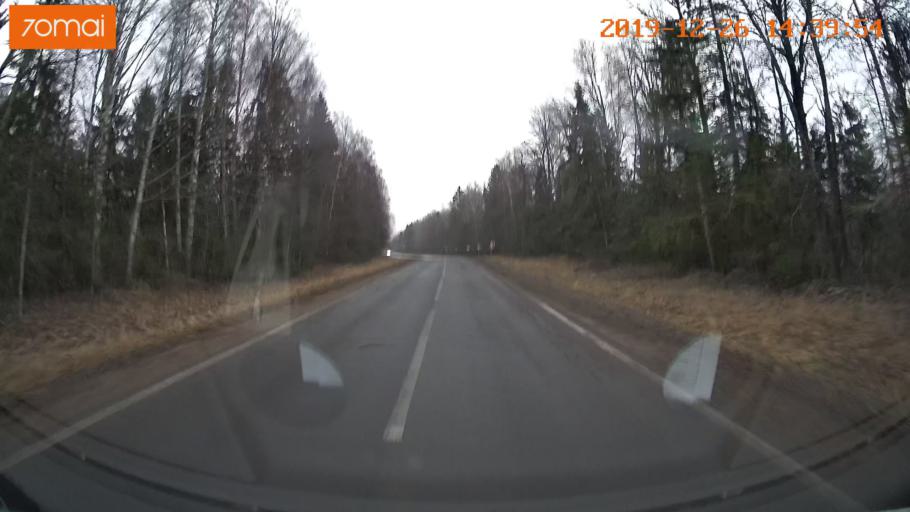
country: RU
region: Jaroslavl
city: Poshekhon'ye
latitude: 58.3793
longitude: 38.9874
